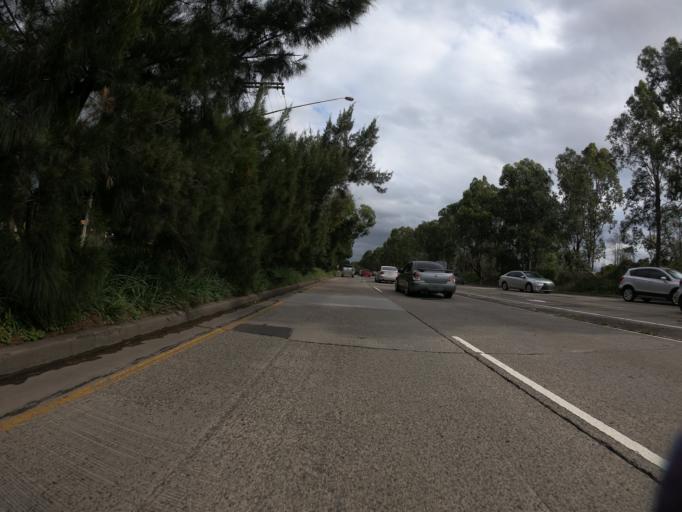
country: AU
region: New South Wales
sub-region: Parramatta
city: Northmead
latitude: -33.7689
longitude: 150.9591
